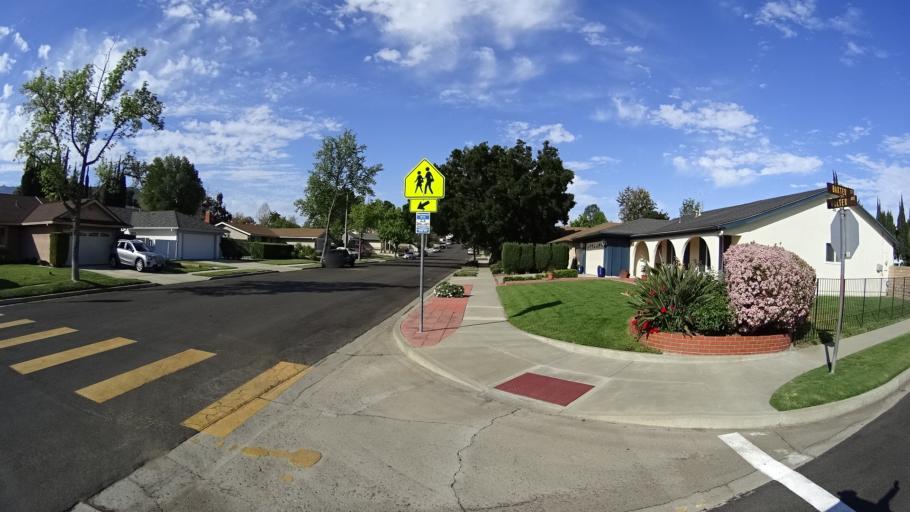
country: US
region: California
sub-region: Ventura County
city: Casa Conejo
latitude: 34.1748
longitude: -118.9511
